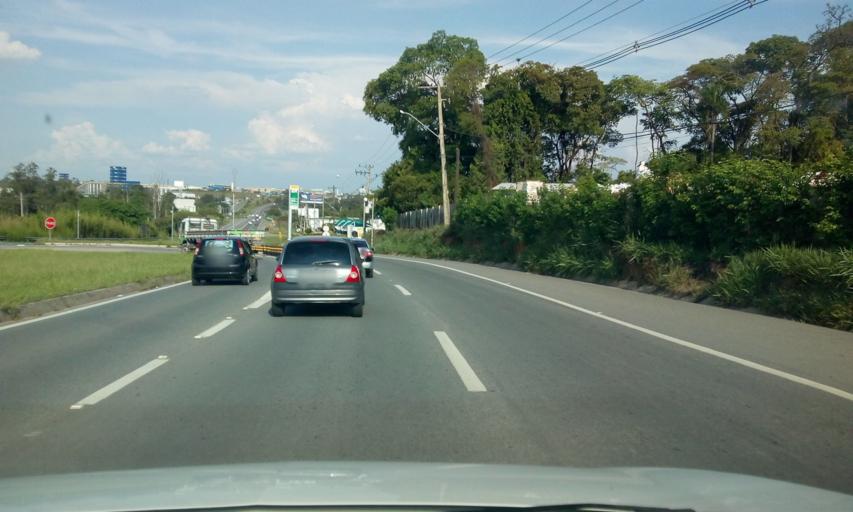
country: BR
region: Sao Paulo
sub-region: Itupeva
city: Itupeva
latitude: -23.1610
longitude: -47.0261
